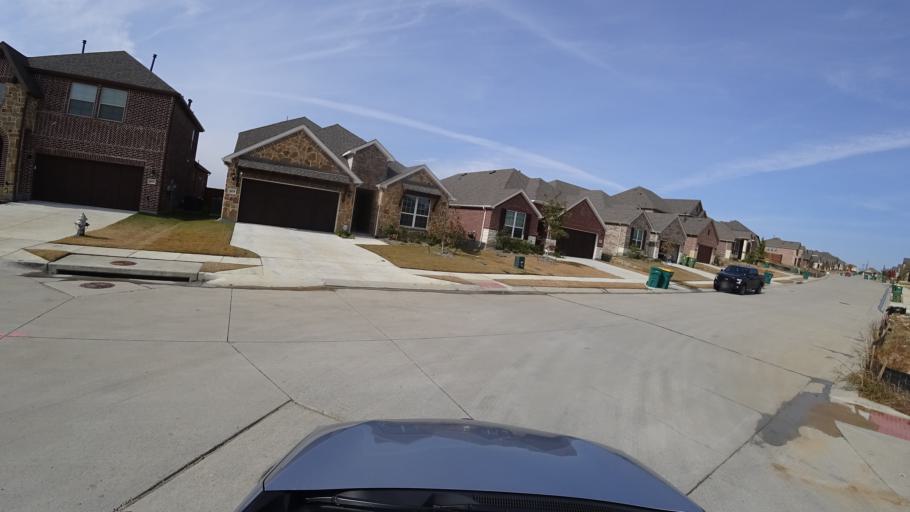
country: US
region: Texas
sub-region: Denton County
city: The Colony
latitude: 33.0530
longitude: -96.8864
